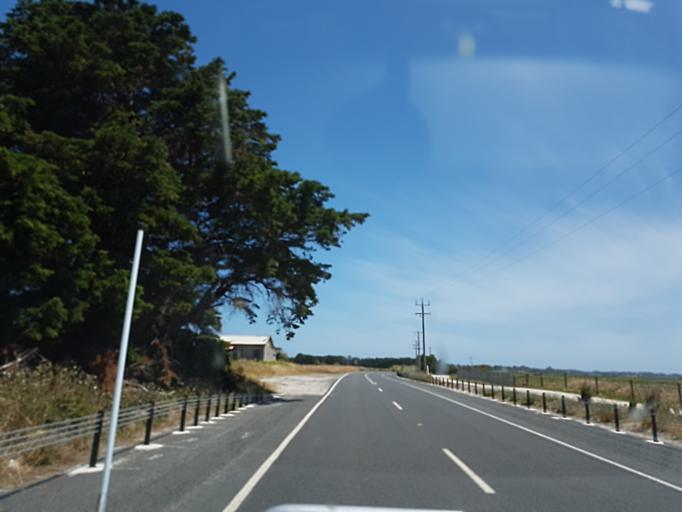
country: AU
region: Victoria
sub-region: Bass Coast
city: North Wonthaggi
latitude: -38.6972
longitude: 145.8601
